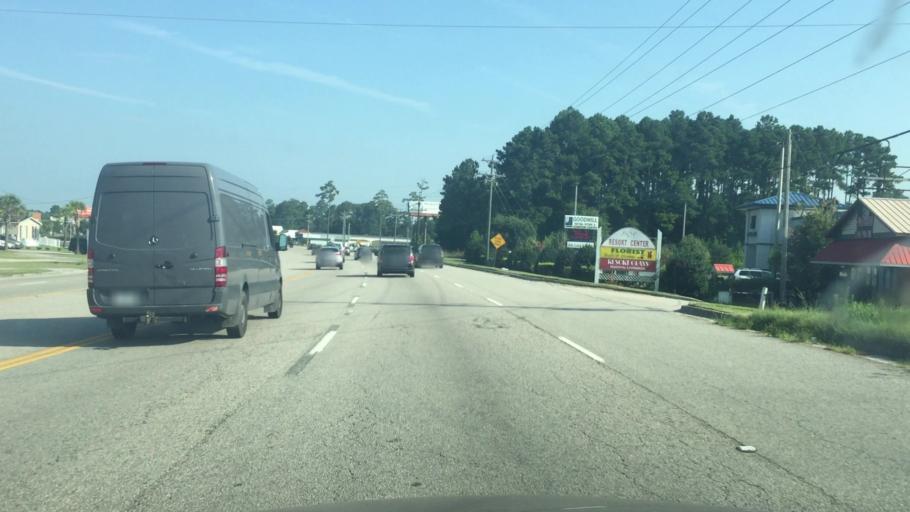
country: US
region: South Carolina
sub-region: Horry County
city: North Myrtle Beach
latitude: 33.8863
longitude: -78.6878
